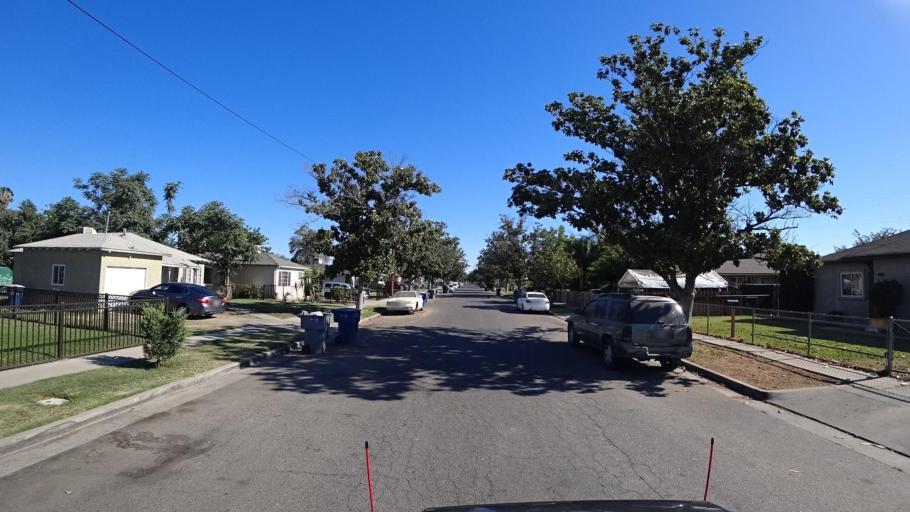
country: US
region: California
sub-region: Fresno County
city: Fresno
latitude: 36.7115
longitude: -119.7863
